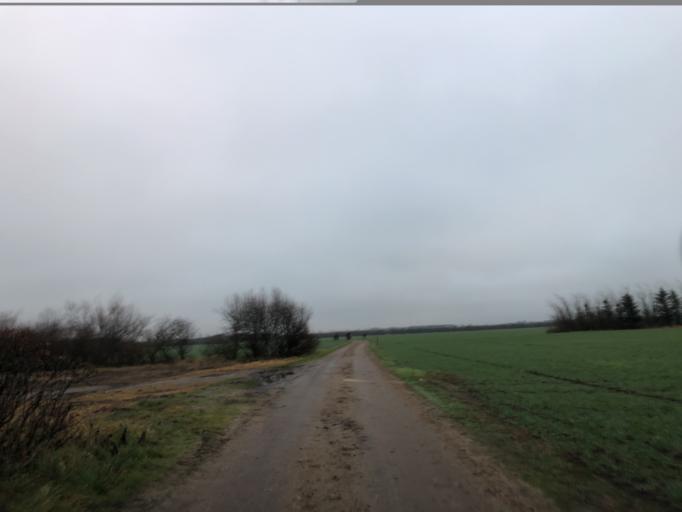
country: DK
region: Central Jutland
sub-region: Ringkobing-Skjern Kommune
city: Ringkobing
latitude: 56.1497
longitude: 8.2424
